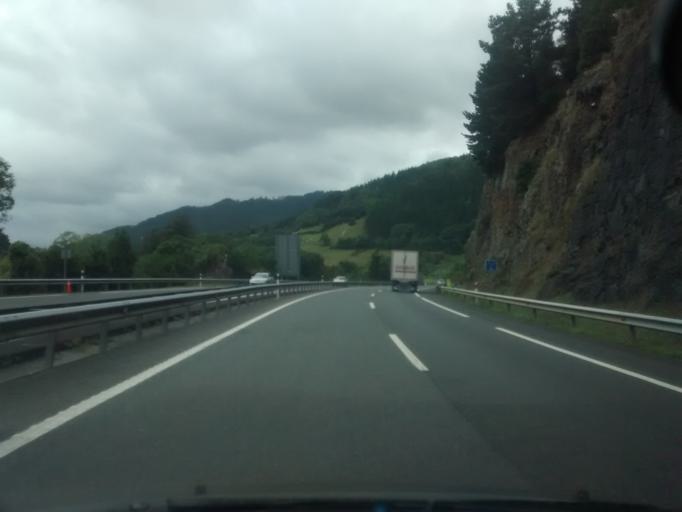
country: ES
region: Basque Country
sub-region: Provincia de Guipuzcoa
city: Mendaro
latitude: 43.2577
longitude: -2.3848
